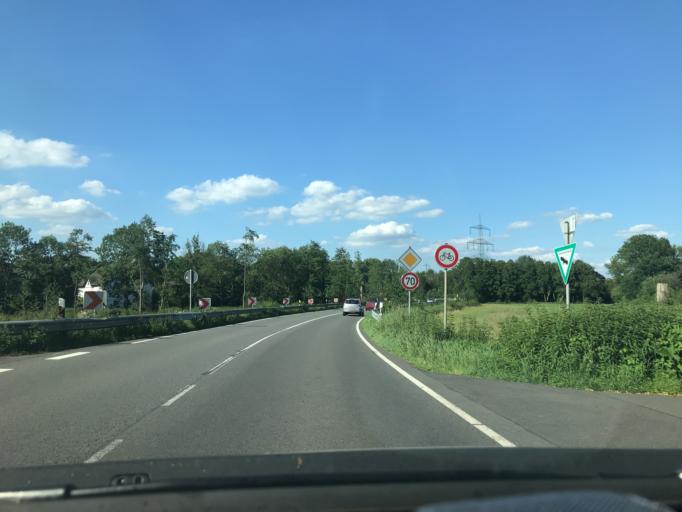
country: DE
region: North Rhine-Westphalia
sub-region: Regierungsbezirk Dusseldorf
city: Neubrueck
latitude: 51.1521
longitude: 6.6794
